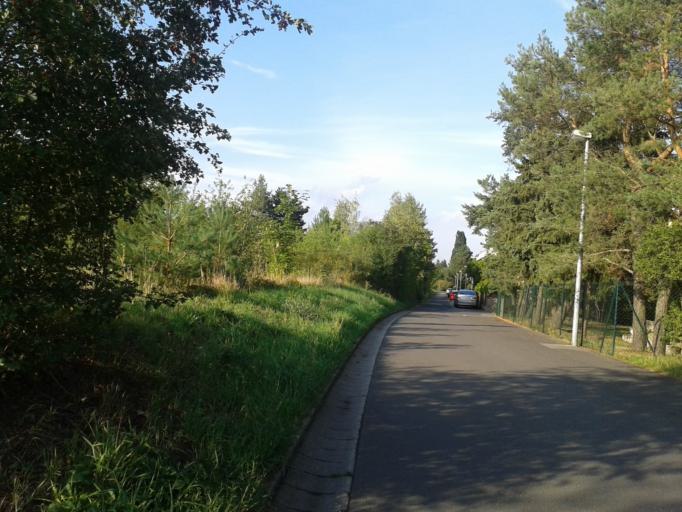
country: DE
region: Bavaria
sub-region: Upper Franconia
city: Gundelsheim
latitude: 49.9206
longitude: 10.9061
